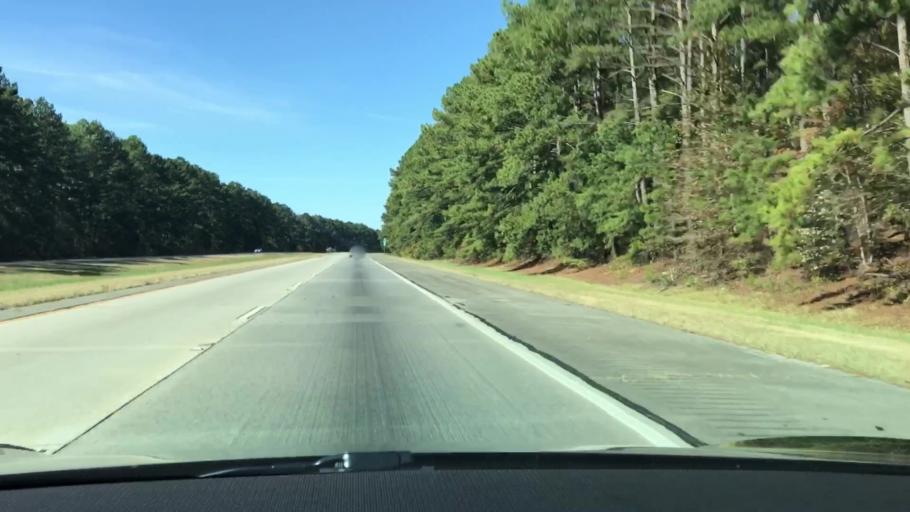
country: US
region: Georgia
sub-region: Taliaferro County
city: Crawfordville
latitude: 33.5313
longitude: -82.9807
